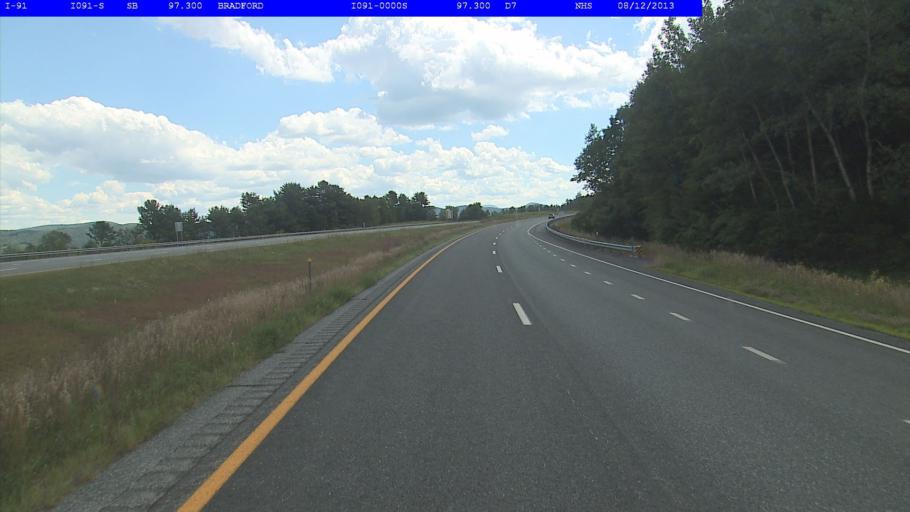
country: US
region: New Hampshire
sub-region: Grafton County
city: Orford
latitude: 43.9802
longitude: -72.1271
